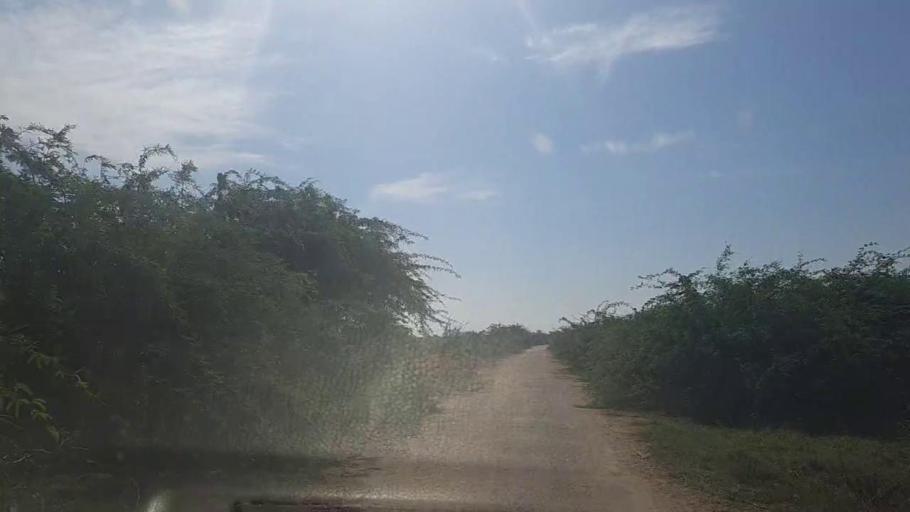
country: PK
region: Sindh
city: Mirpur Batoro
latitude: 24.6716
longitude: 68.1832
